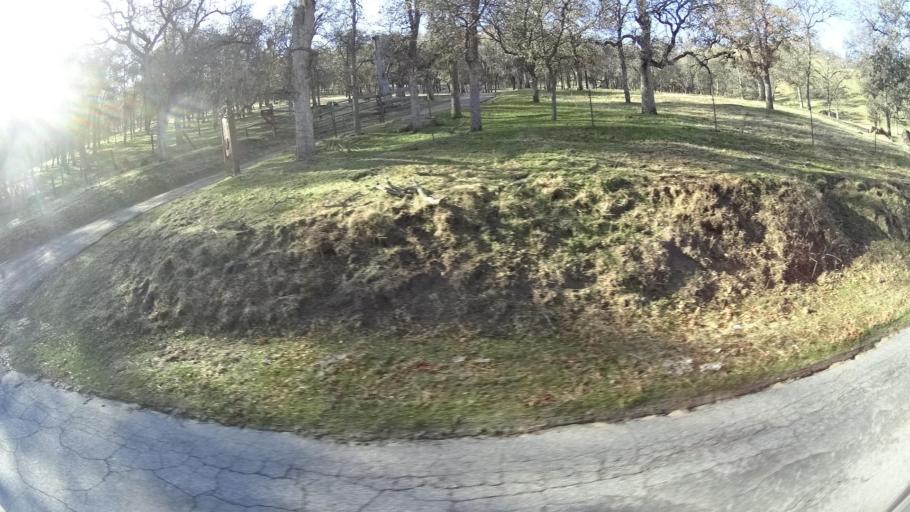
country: US
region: California
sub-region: Kern County
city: Alta Sierra
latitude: 35.7676
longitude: -118.8244
